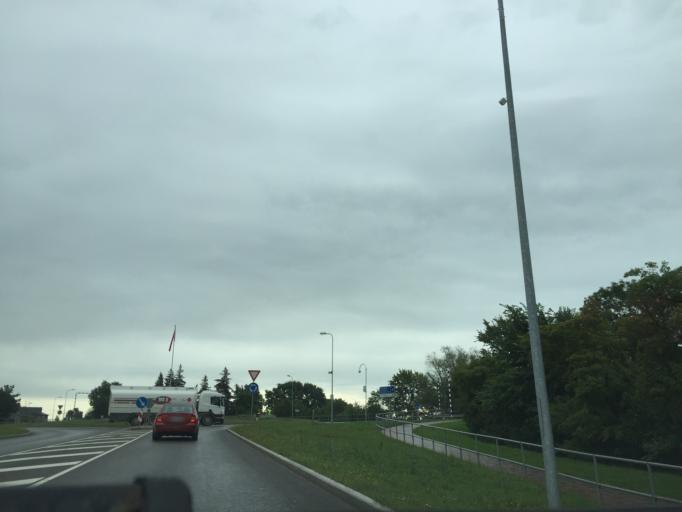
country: LV
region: Jekabpils Rajons
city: Jekabpils
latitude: 56.5016
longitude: 25.8772
